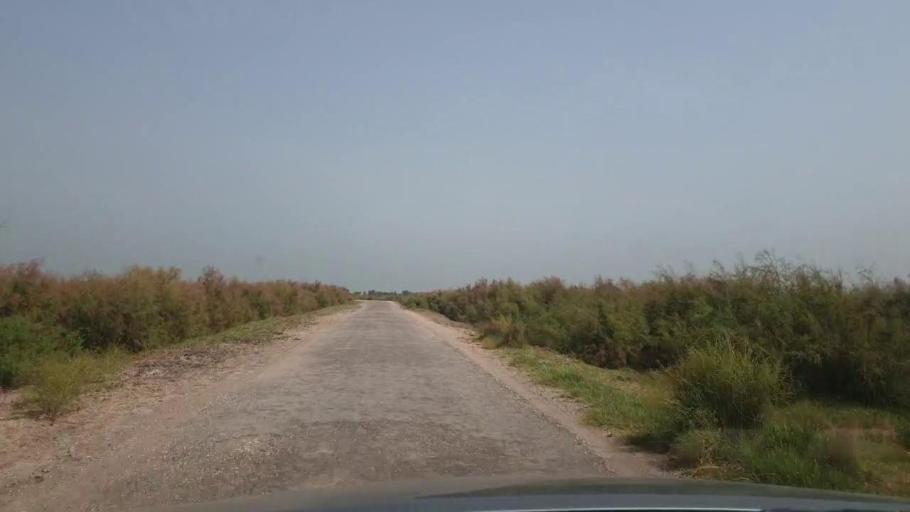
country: PK
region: Sindh
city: Madeji
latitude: 27.8311
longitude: 68.4469
